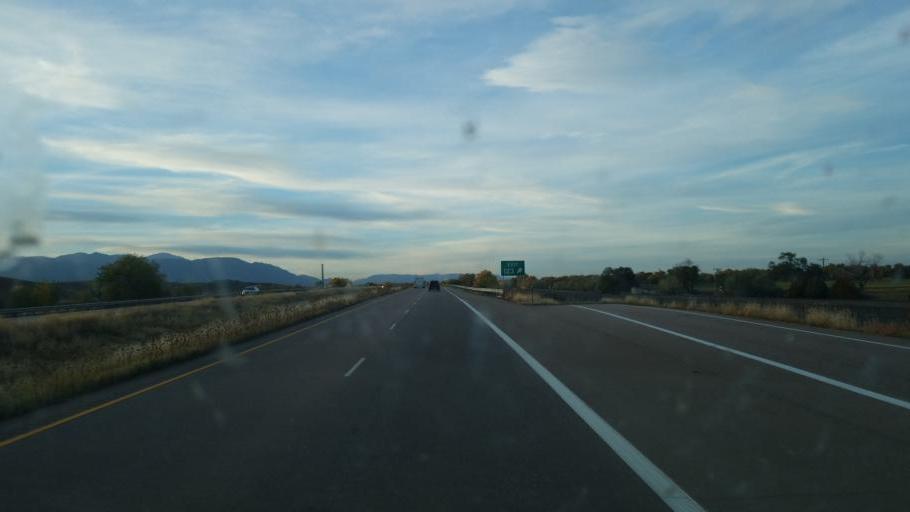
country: US
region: Colorado
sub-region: El Paso County
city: Fountain
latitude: 38.6073
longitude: -104.6808
